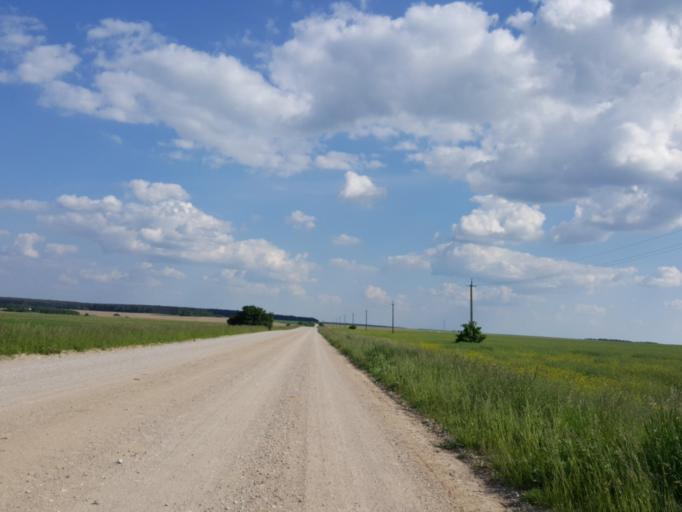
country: BY
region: Brest
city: Kamyanyets
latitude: 52.4421
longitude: 23.6172
